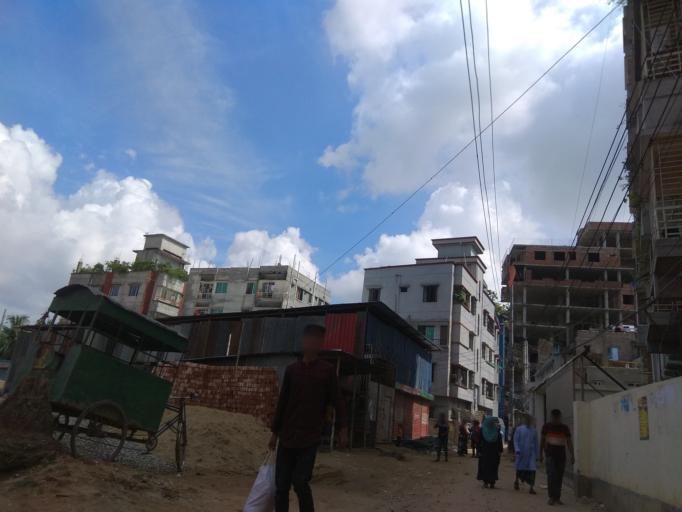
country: BD
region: Dhaka
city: Tungi
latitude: 23.8137
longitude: 90.3923
